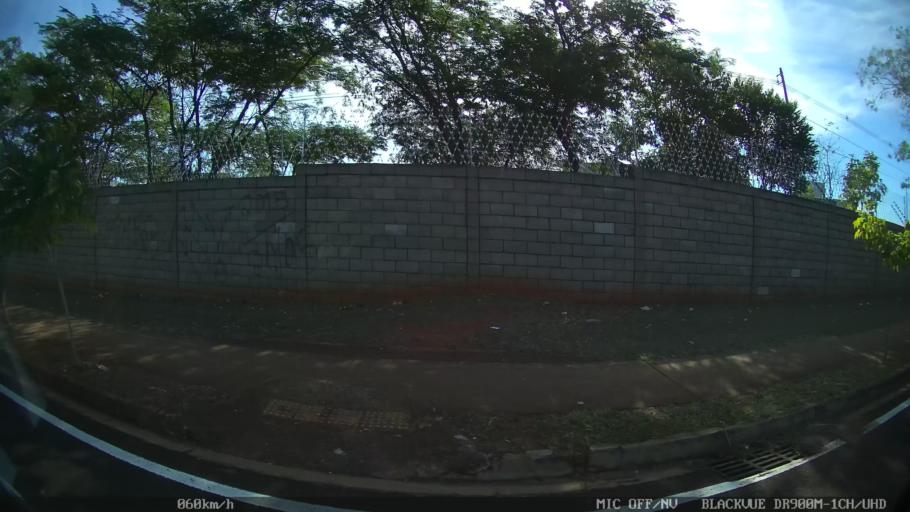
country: BR
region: Sao Paulo
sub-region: Sao Jose Do Rio Preto
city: Sao Jose do Rio Preto
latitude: -20.8078
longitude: -49.3334
